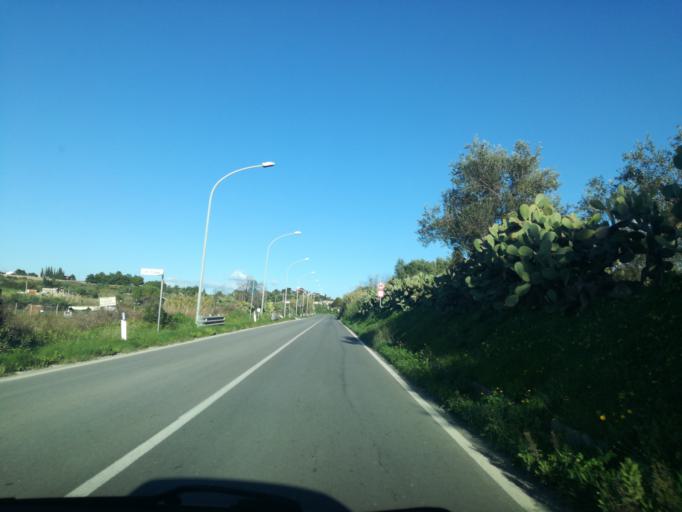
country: IT
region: Sicily
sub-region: Provincia di Caltanissetta
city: Gela
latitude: 37.1045
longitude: 14.1588
